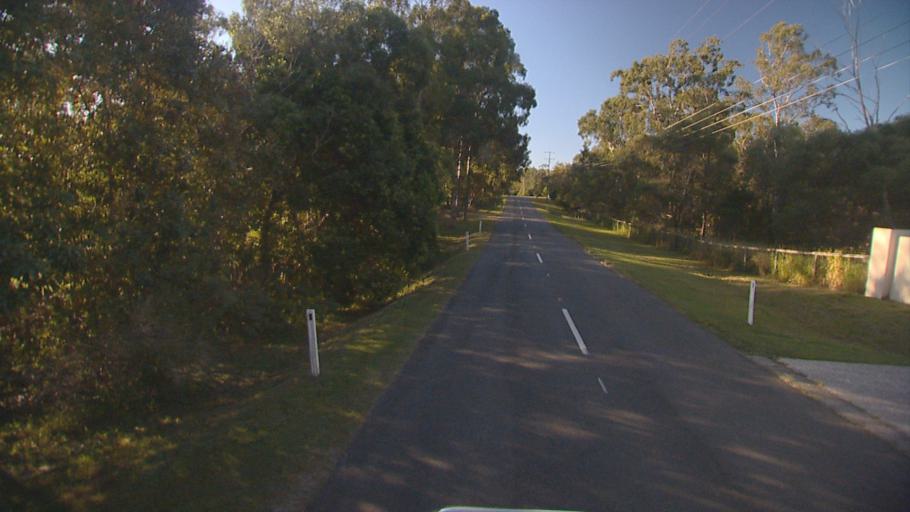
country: AU
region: Queensland
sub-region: Redland
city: Redland Bay
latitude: -27.6766
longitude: 153.2759
